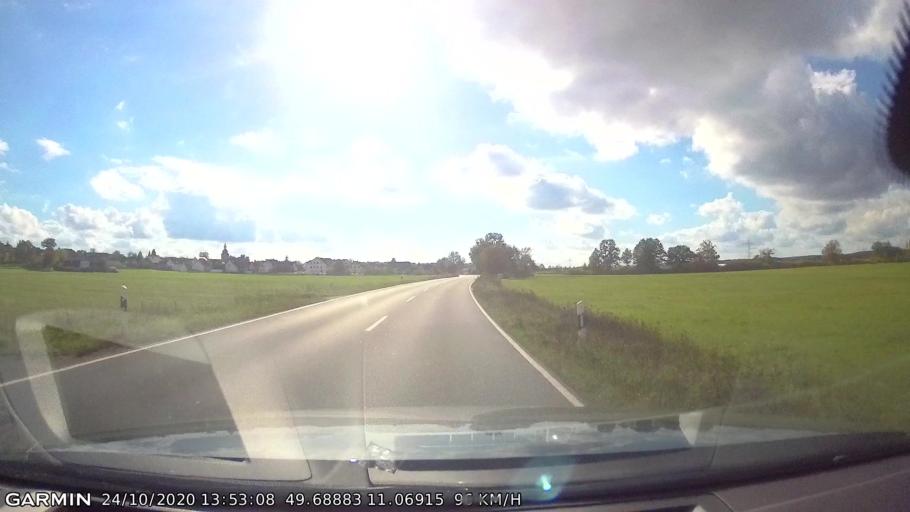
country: DE
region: Bavaria
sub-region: Upper Franconia
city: Poxdorf
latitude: 49.6886
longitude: 11.0690
